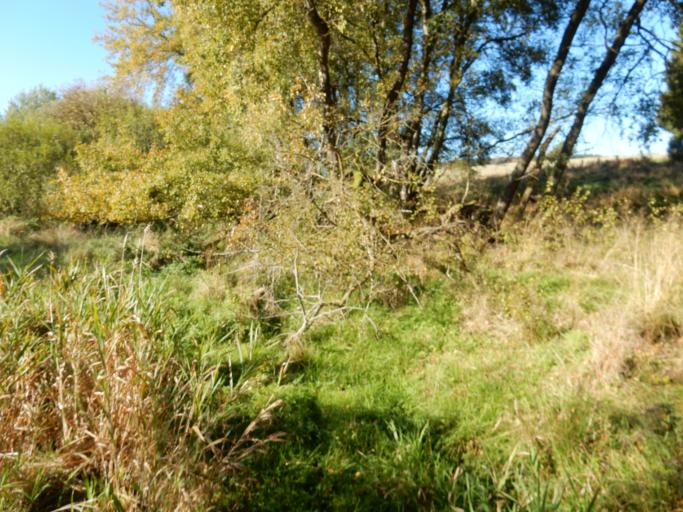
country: LU
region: Diekirch
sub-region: Canton de Clervaux
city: Troisvierges
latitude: 50.1339
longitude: 5.9739
